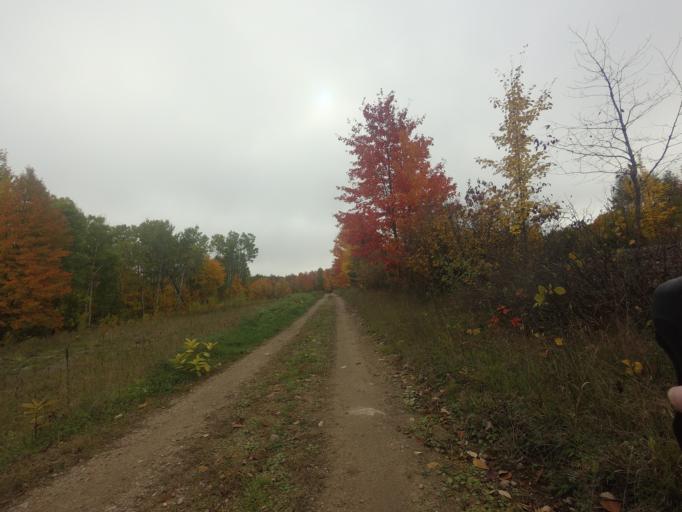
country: CA
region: Ontario
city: Pembroke
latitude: 45.7296
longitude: -77.2276
